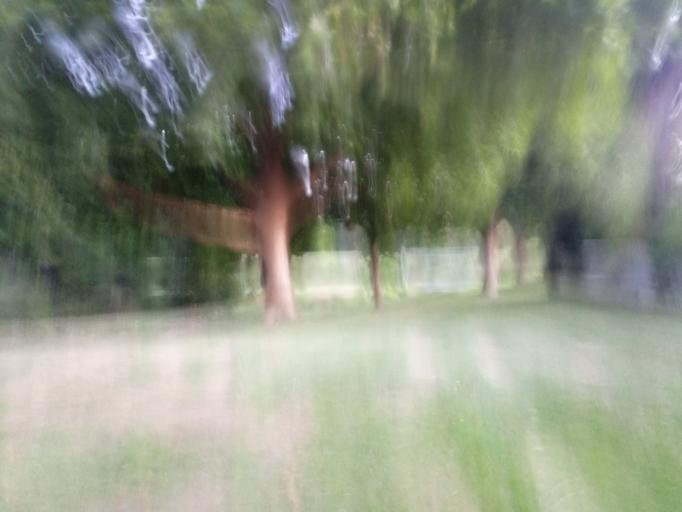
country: NZ
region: Gisborne
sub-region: Gisborne District
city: Gisborne
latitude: -38.6461
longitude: 177.9925
